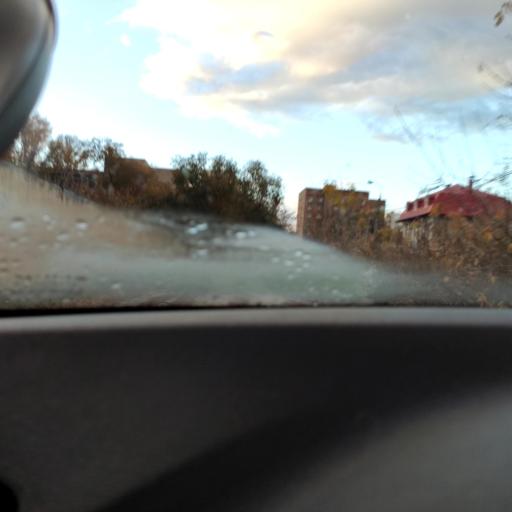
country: RU
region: Samara
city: Smyshlyayevka
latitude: 53.2050
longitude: 50.2850
